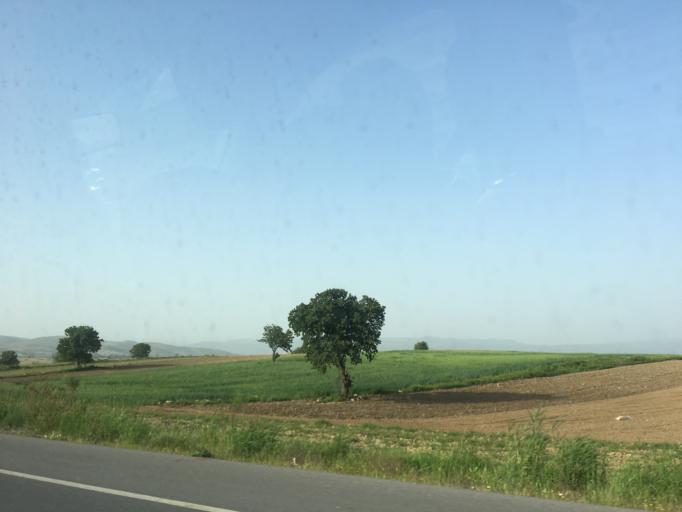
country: TR
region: Manisa
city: Golmarmara
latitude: 38.6248
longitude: 27.9352
